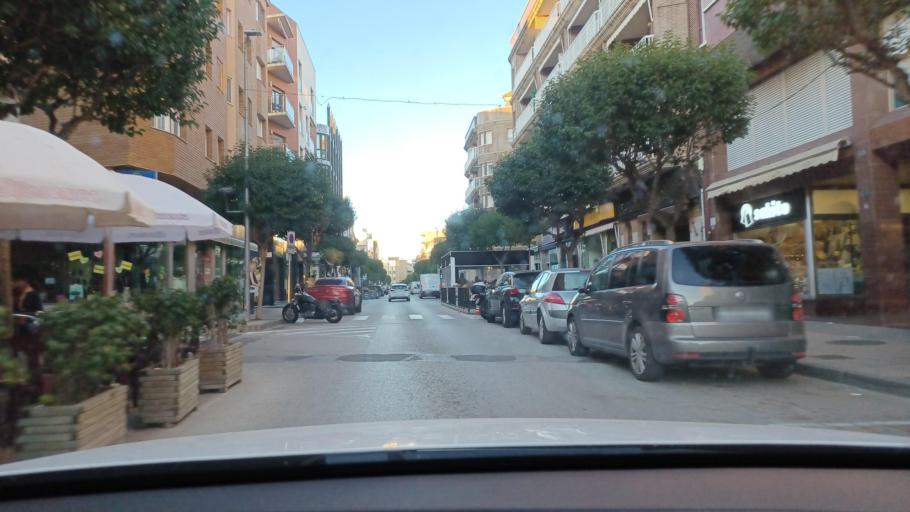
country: ES
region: Catalonia
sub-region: Provincia de Tarragona
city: Amposta
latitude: 40.7094
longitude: 0.5799
